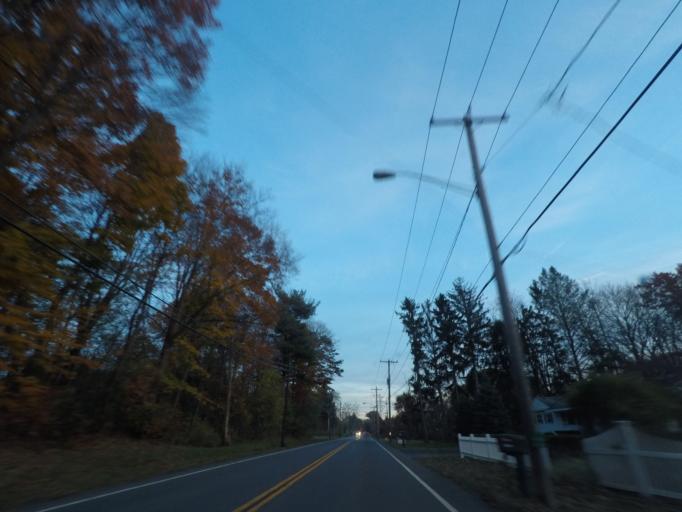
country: US
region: New York
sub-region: Schenectady County
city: Rotterdam
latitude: 42.7633
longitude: -73.9367
